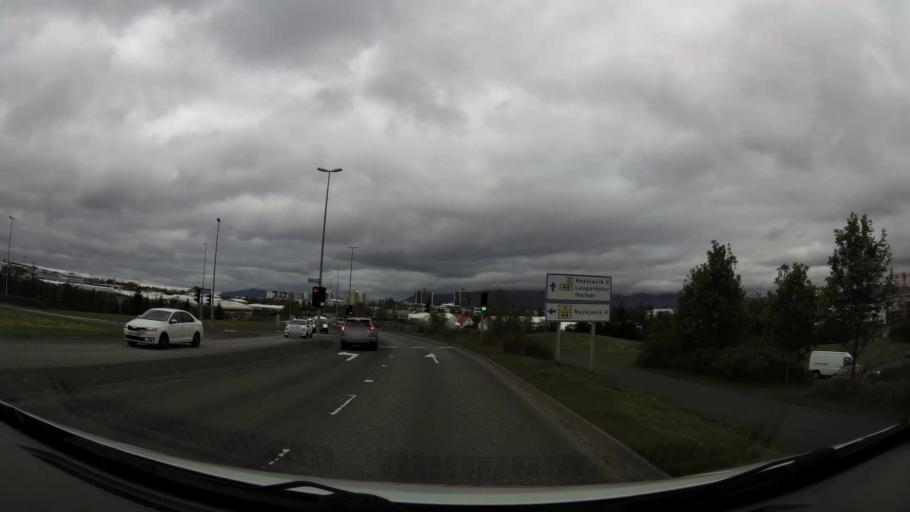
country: IS
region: Capital Region
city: Reykjavik
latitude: 64.1265
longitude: -21.8631
